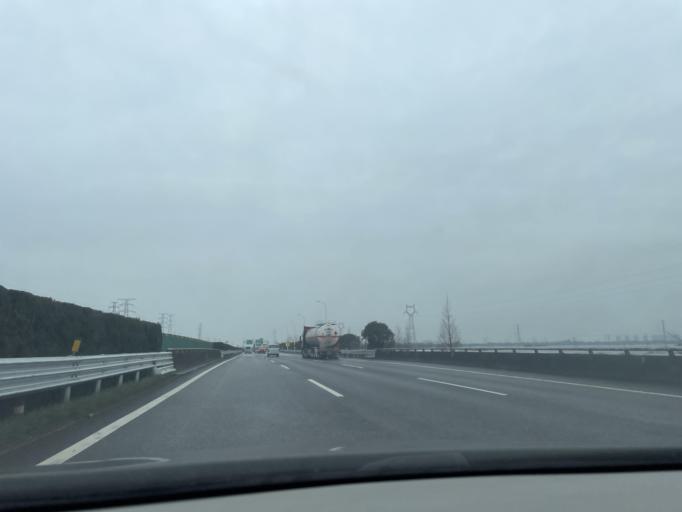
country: CN
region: Zhejiang Sheng
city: Xinpu
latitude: 30.2704
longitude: 121.3386
